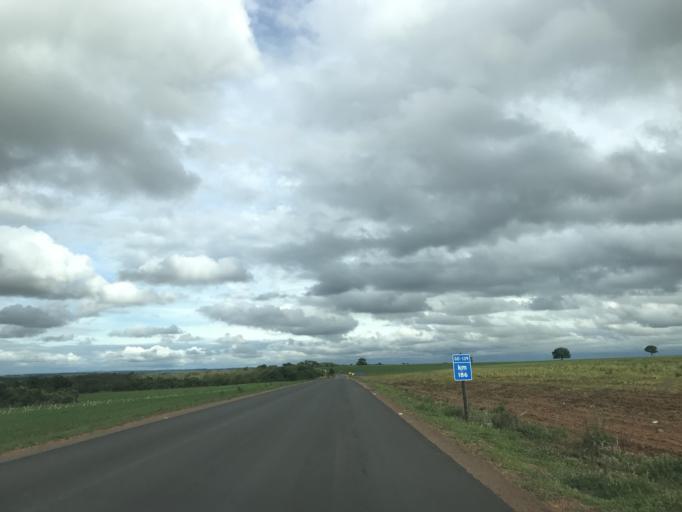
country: BR
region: Goias
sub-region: Vianopolis
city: Vianopolis
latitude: -16.9673
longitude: -48.6091
